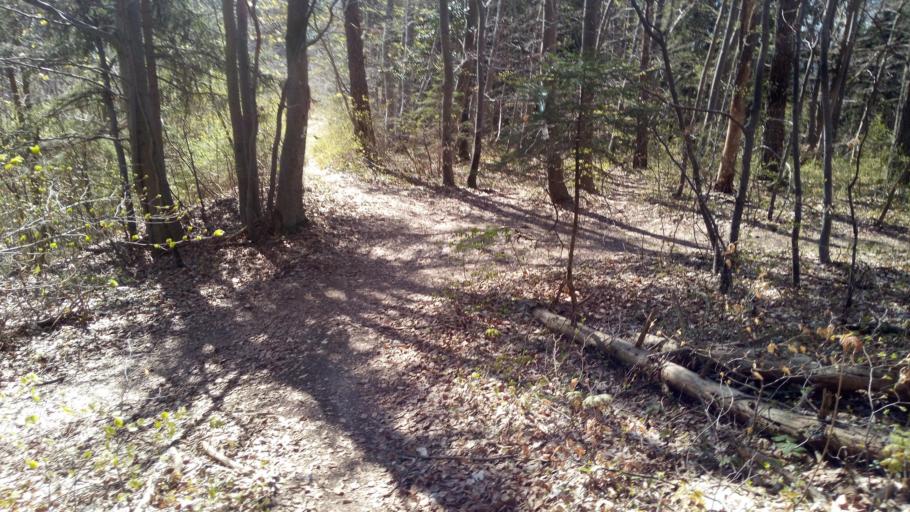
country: DE
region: Baden-Wuerttemberg
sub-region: Regierungsbezirk Stuttgart
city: Donzdorf
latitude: 48.7121
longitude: 9.8428
